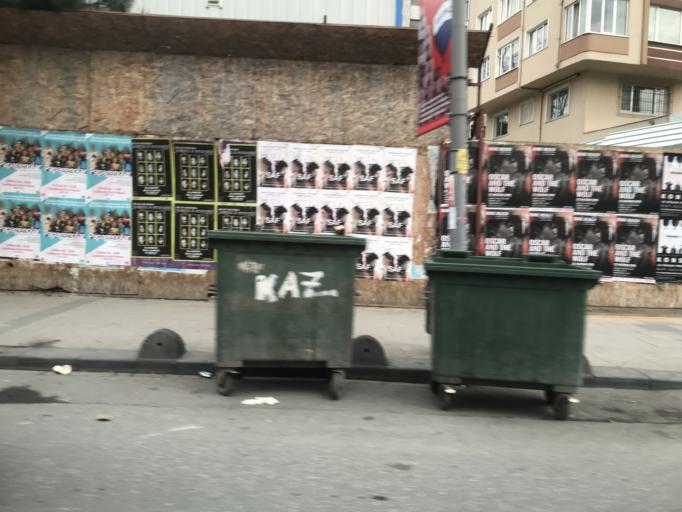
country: TR
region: Istanbul
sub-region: Atasehir
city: Atasehir
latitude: 40.9711
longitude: 29.0838
